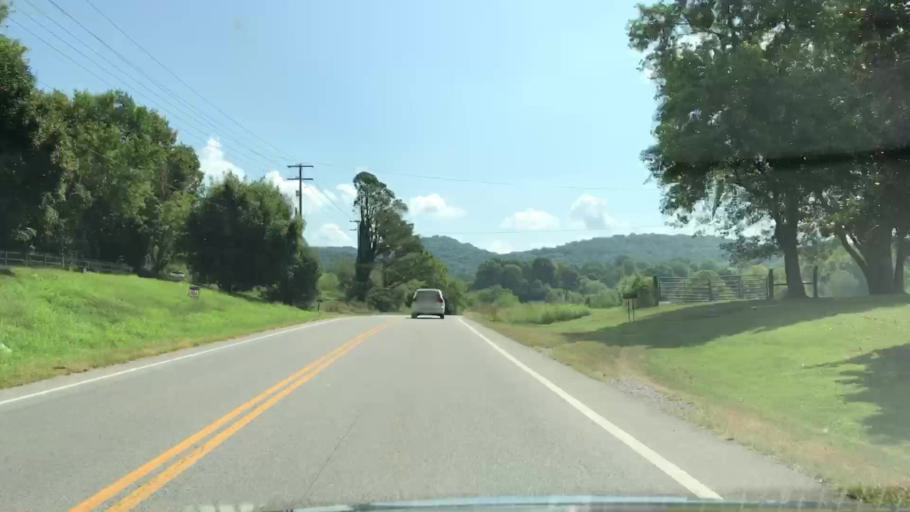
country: US
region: Tennessee
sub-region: Trousdale County
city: Hartsville
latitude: 36.3838
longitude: -86.1223
